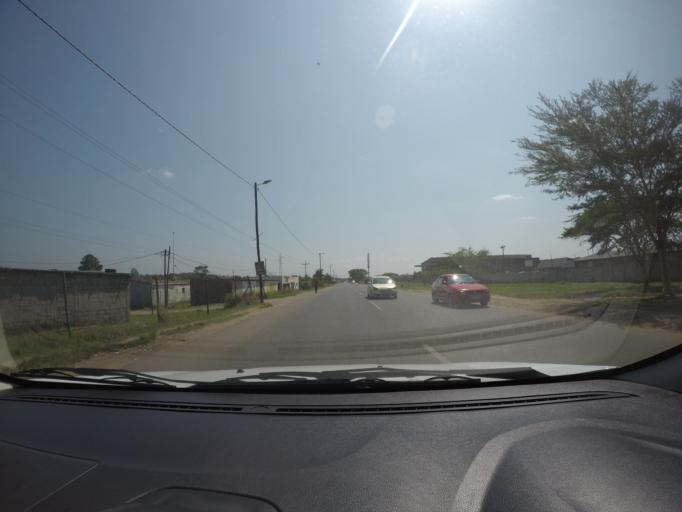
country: ZA
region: KwaZulu-Natal
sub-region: uThungulu District Municipality
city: eSikhawini
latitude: -28.8635
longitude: 31.9080
